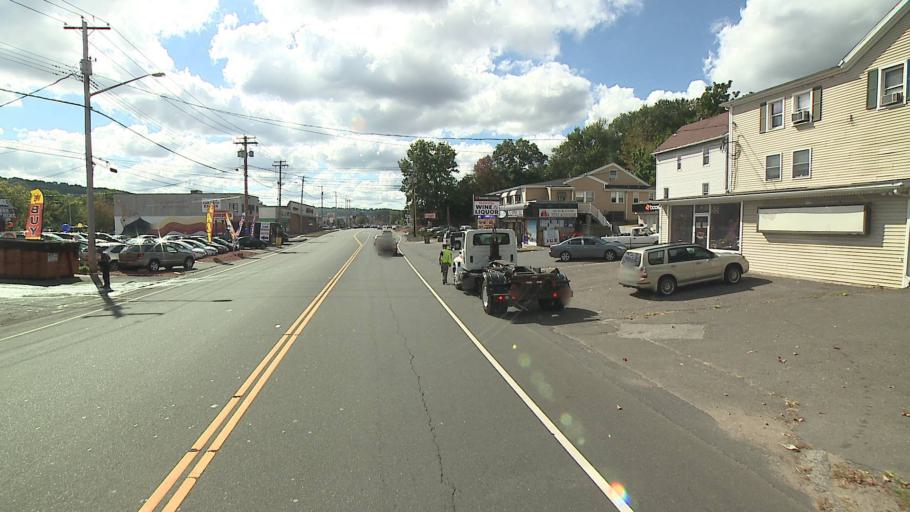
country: US
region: Connecticut
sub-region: New Haven County
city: Ansonia
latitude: 41.3348
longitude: -73.0835
